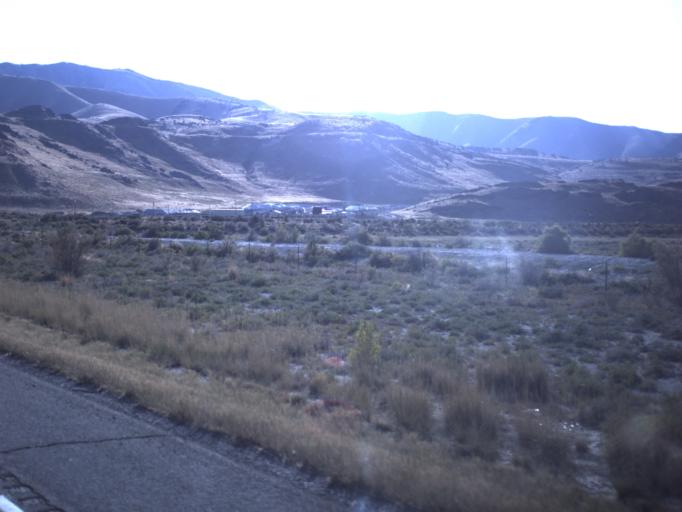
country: US
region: Utah
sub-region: Tooele County
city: Grantsville
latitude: 40.6828
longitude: -112.5461
